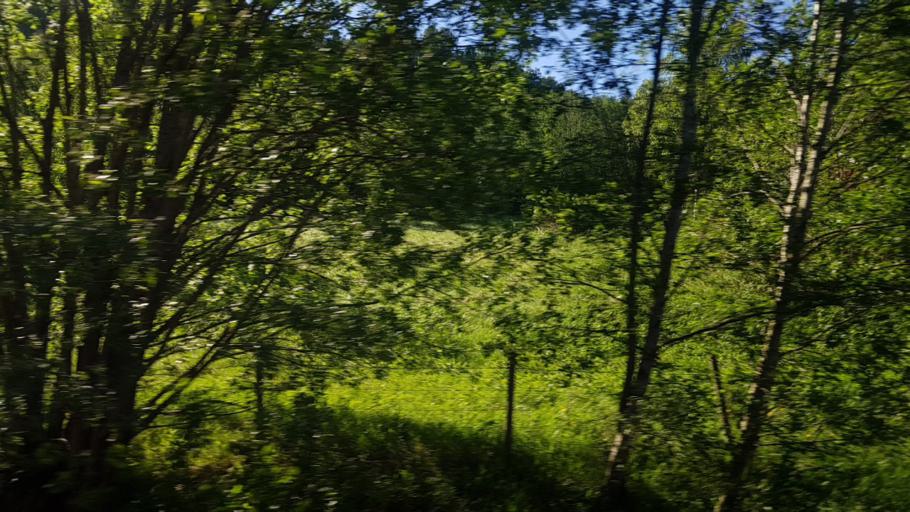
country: NO
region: Sor-Trondelag
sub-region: Melhus
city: Lundamo
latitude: 63.1390
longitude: 10.2592
